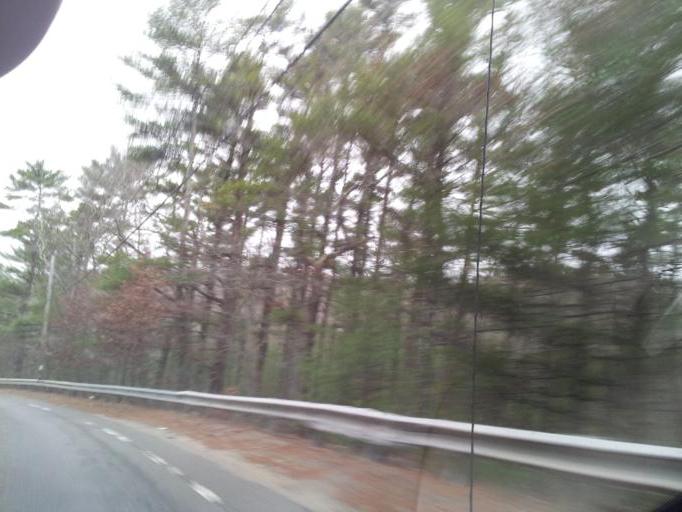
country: US
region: Massachusetts
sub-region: Plymouth County
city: Plymouth
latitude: 41.9372
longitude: -70.5950
